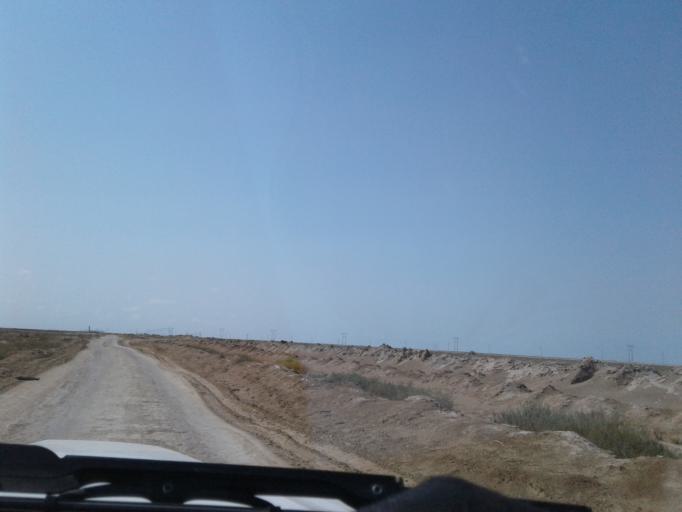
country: IR
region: Golestan
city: Gomishan
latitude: 37.8282
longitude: 53.9215
